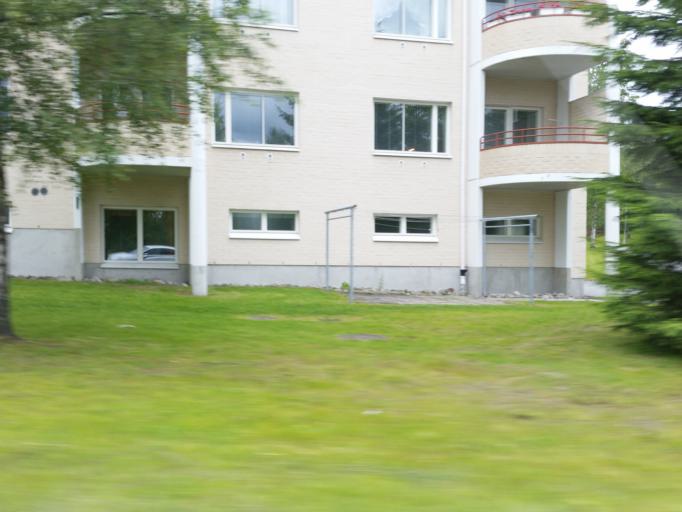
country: FI
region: Northern Savo
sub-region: Kuopio
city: Kuopio
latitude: 62.9039
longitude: 27.7059
